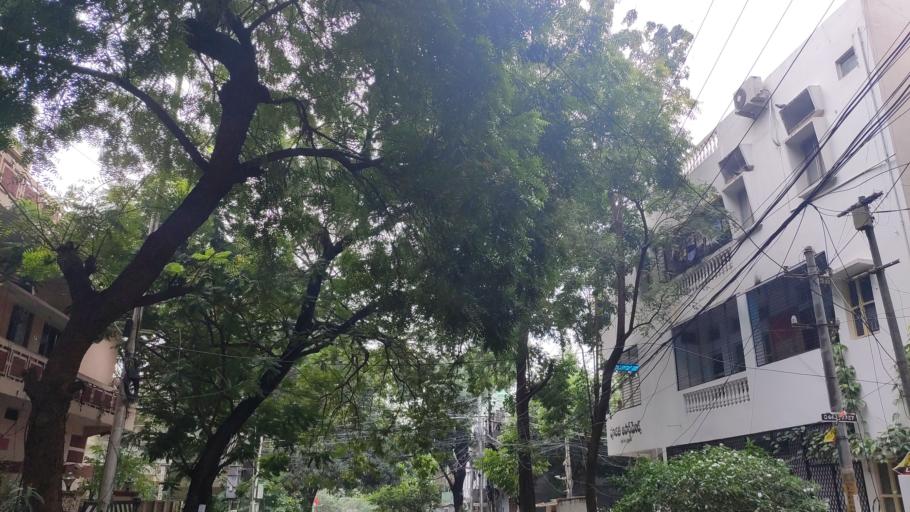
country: IN
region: Telangana
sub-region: Rangareddi
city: Kukatpalli
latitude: 17.4431
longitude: 78.4335
